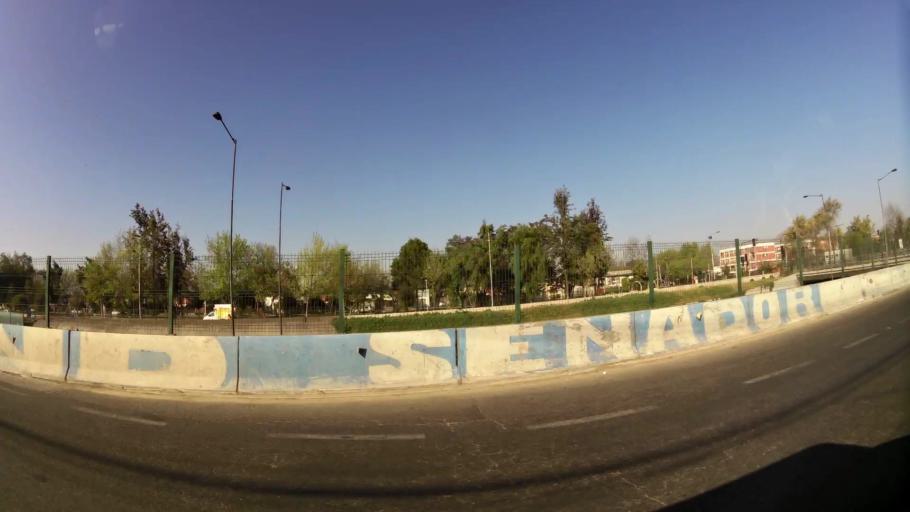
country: CL
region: Santiago Metropolitan
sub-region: Provincia de Santiago
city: Santiago
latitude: -33.3765
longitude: -70.6560
